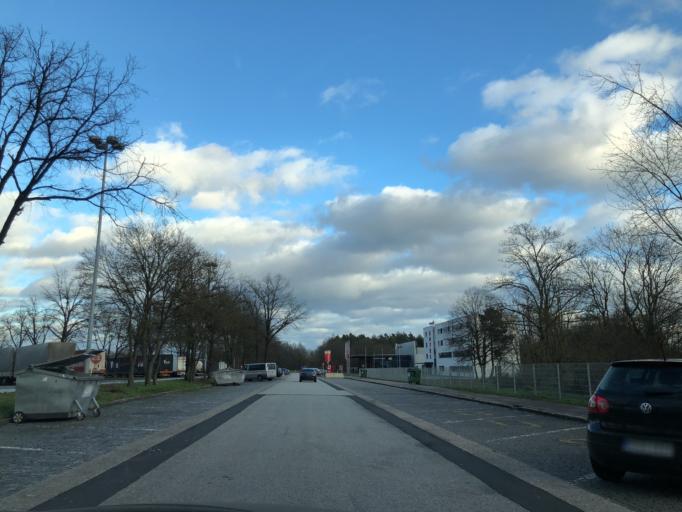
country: DE
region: Bavaria
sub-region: Regierungsbezirk Mittelfranken
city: Wachenroth
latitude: 49.7307
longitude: 10.7249
